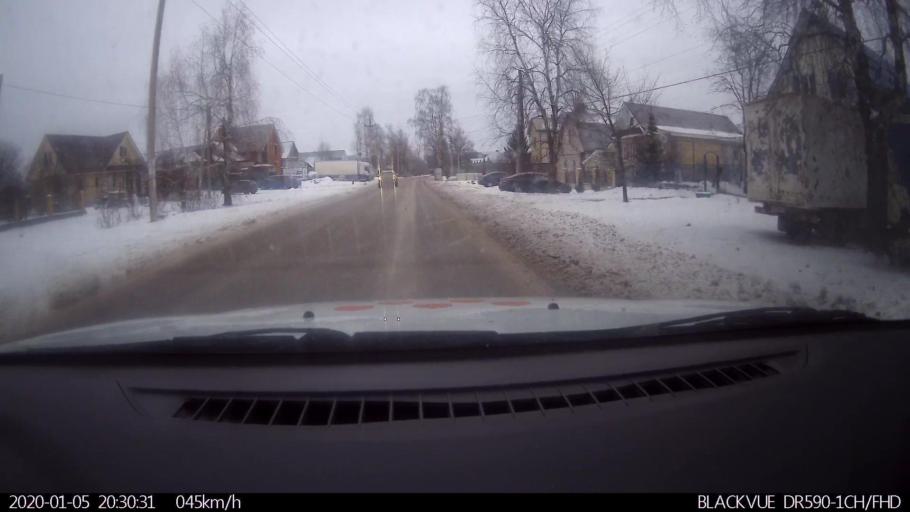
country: RU
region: Nizjnij Novgorod
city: Lukino
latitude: 56.3994
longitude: 43.7298
